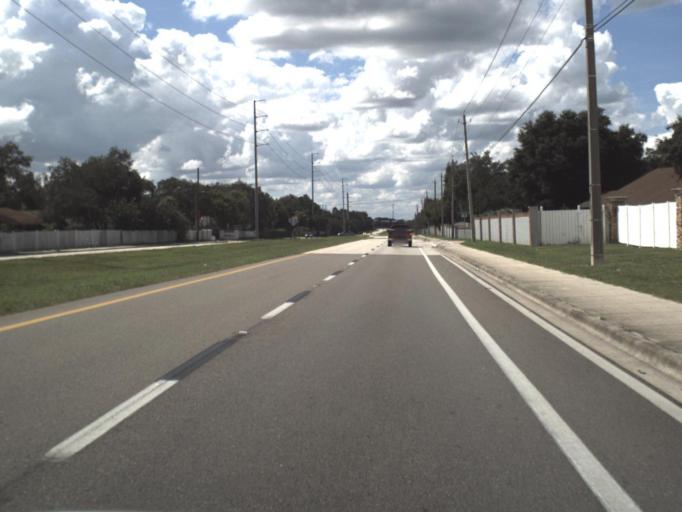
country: US
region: Florida
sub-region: Polk County
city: Jan-Phyl Village
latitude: 28.0059
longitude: -81.7870
